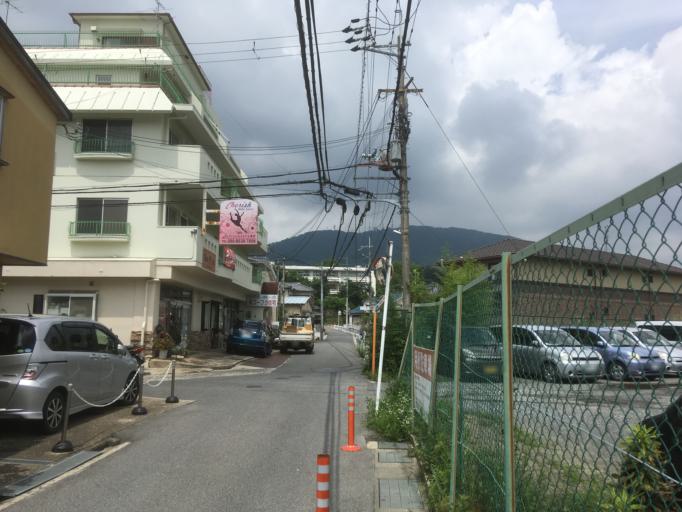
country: JP
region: Nara
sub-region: Ikoma-shi
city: Ikoma
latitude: 34.6648
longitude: 135.7082
